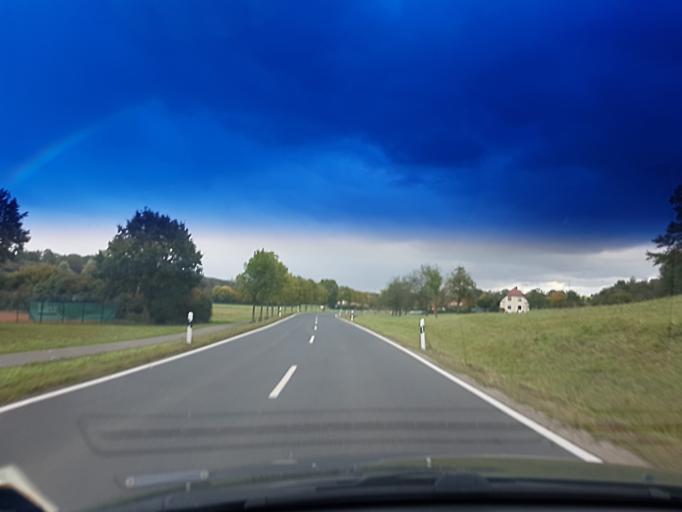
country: DE
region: Bavaria
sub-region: Regierungsbezirk Mittelfranken
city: Burghaslach
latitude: 49.7303
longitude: 10.6108
